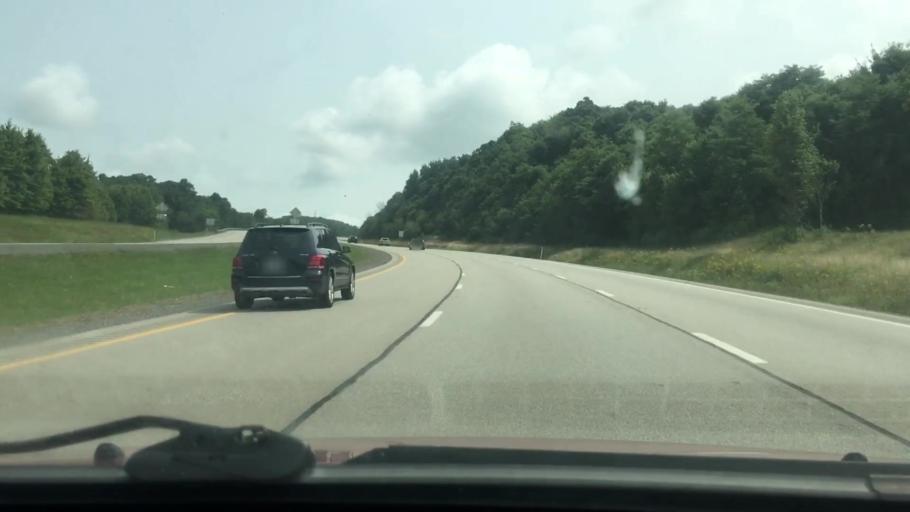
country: US
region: West Virginia
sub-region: Preston County
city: Terra Alta
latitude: 39.6575
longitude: -79.5107
